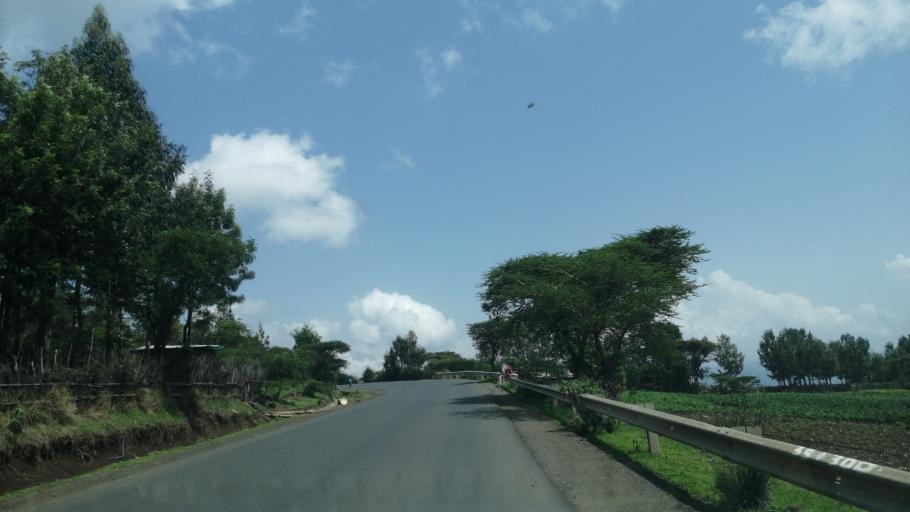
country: ET
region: Oromiya
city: Guder
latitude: 8.9942
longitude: 37.6228
